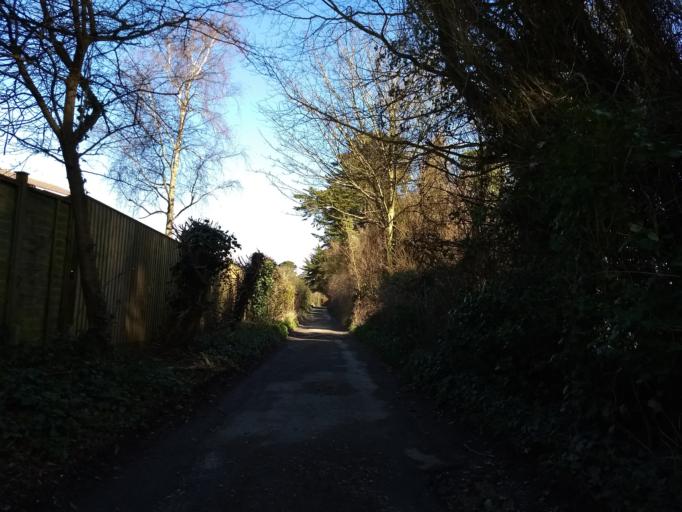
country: GB
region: England
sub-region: Isle of Wight
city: Seaview
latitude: 50.7094
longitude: -1.1080
